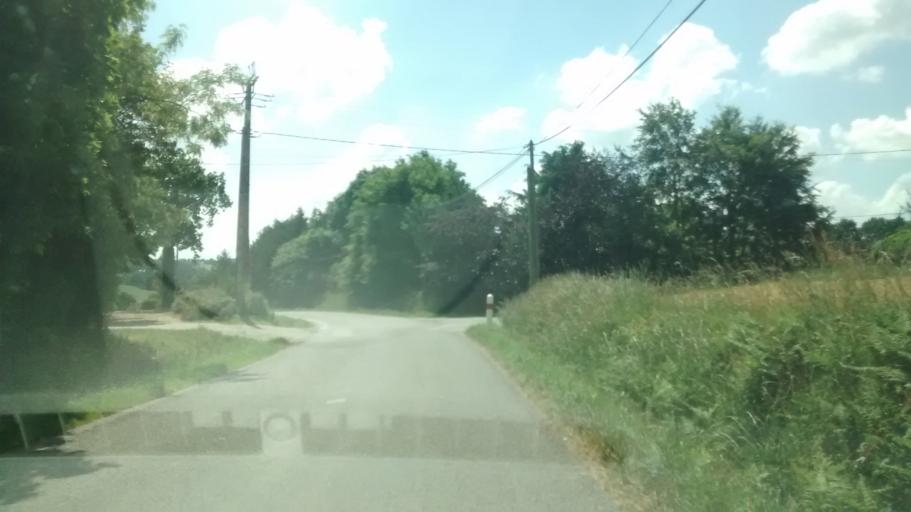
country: FR
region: Brittany
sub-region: Departement du Morbihan
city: Caro
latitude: 47.8753
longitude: -2.2987
